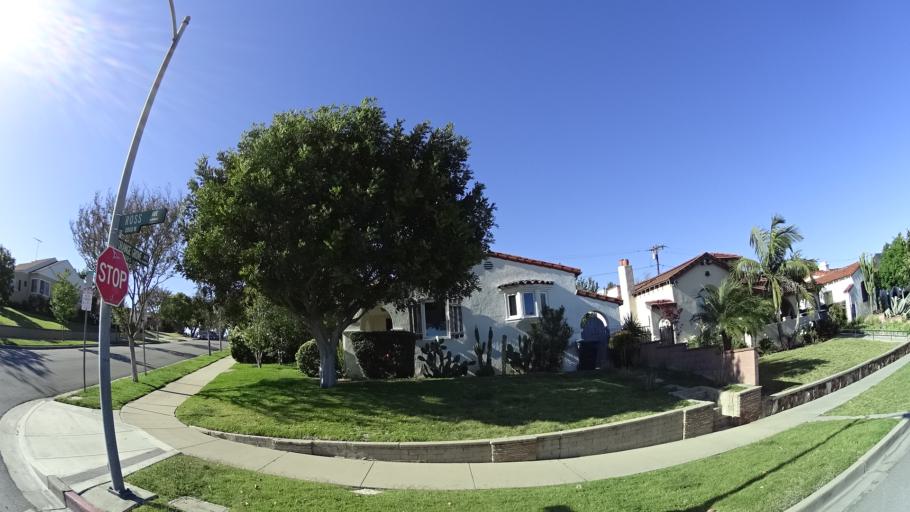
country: US
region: California
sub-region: Los Angeles County
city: Belvedere
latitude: 34.0705
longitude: -118.1560
